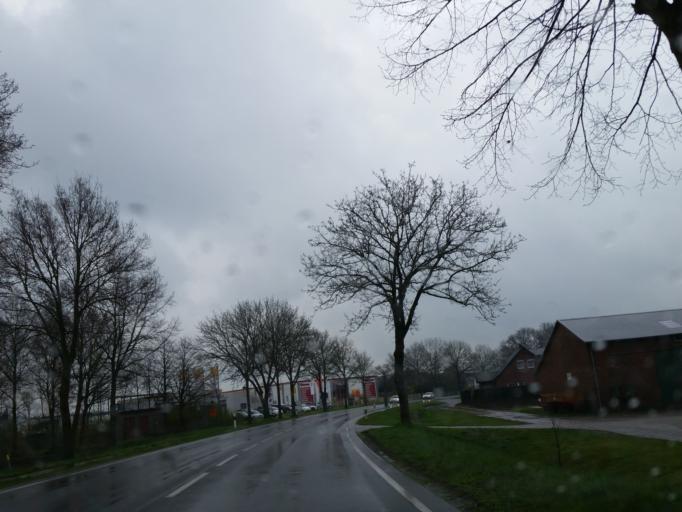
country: DE
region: Lower Saxony
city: Bei der Hohne
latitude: 53.4982
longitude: 9.1048
